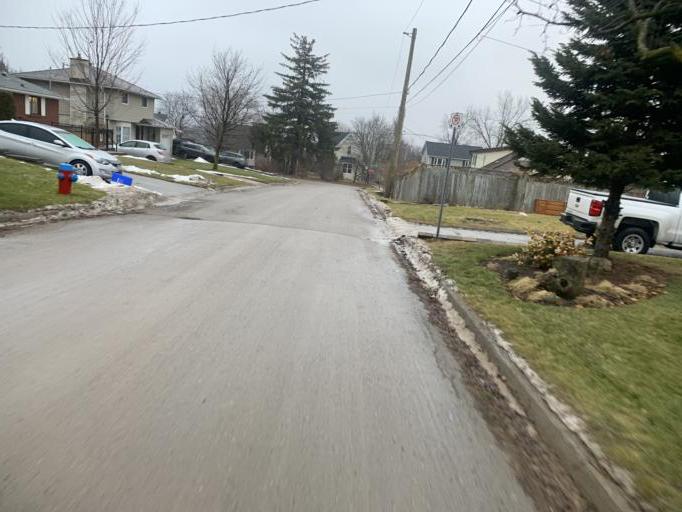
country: CA
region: Ontario
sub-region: Halton
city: Milton
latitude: 43.6538
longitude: -79.9304
